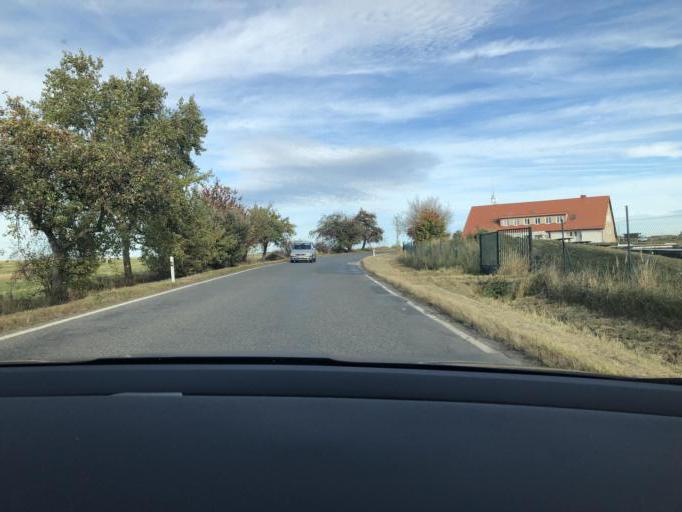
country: CZ
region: Central Bohemia
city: Divisov
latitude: 49.7899
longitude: 14.8635
